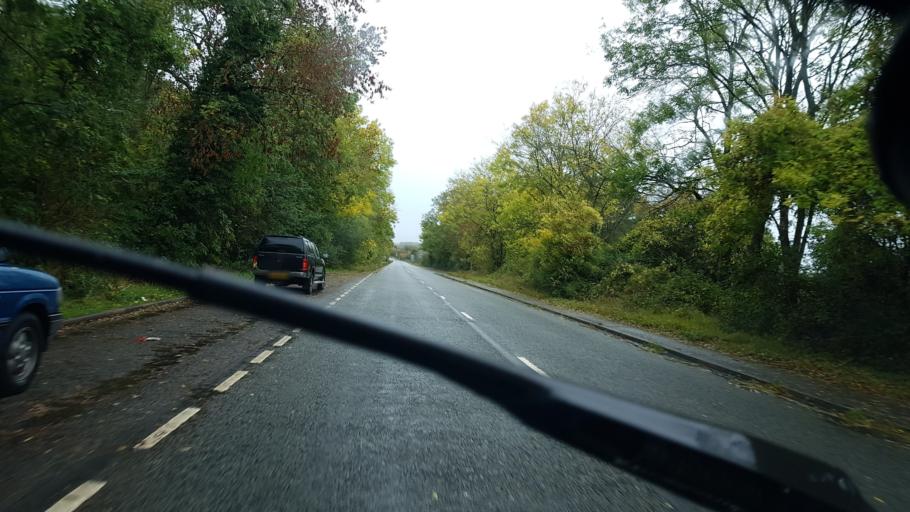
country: GB
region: England
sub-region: Gloucestershire
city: Tewkesbury
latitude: 52.0379
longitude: -2.1662
